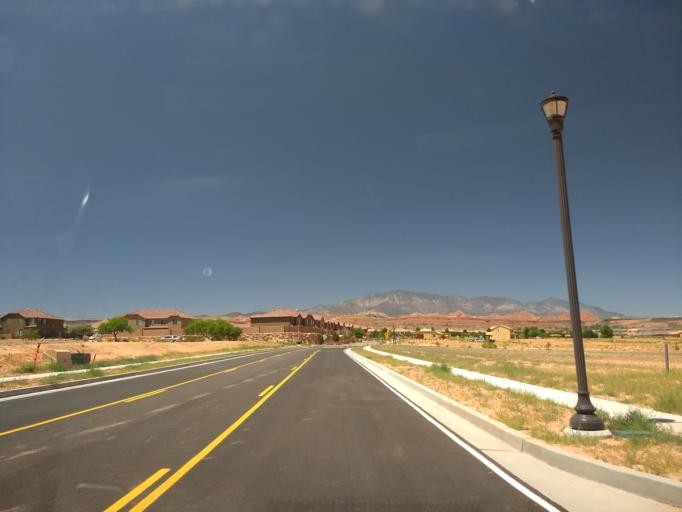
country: US
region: Utah
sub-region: Washington County
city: Washington
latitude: 37.1334
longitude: -113.4838
